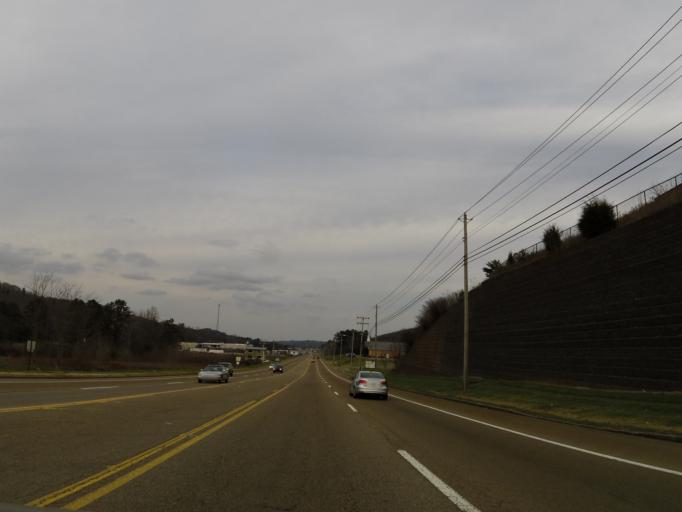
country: US
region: Tennessee
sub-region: Rhea County
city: Graysville
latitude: 35.4611
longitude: -85.0452
